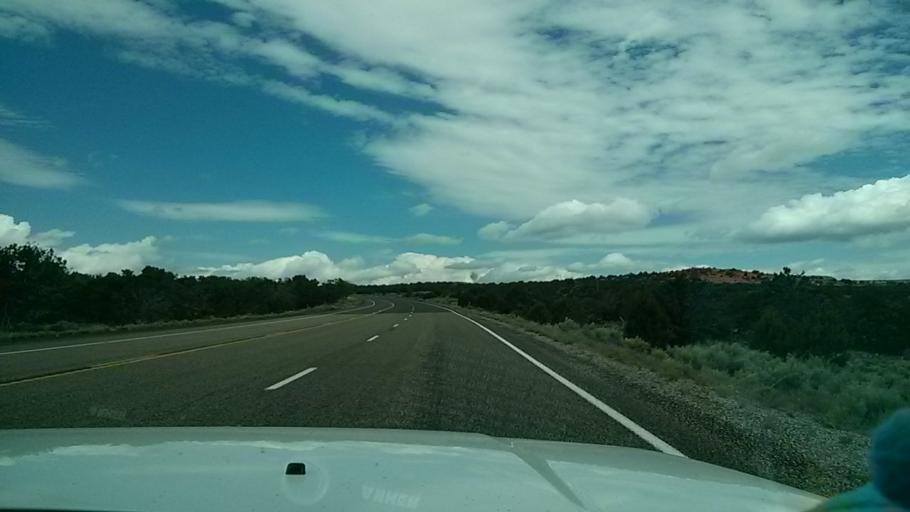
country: US
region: Utah
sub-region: Kane County
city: Kanab
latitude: 37.1506
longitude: -112.5710
